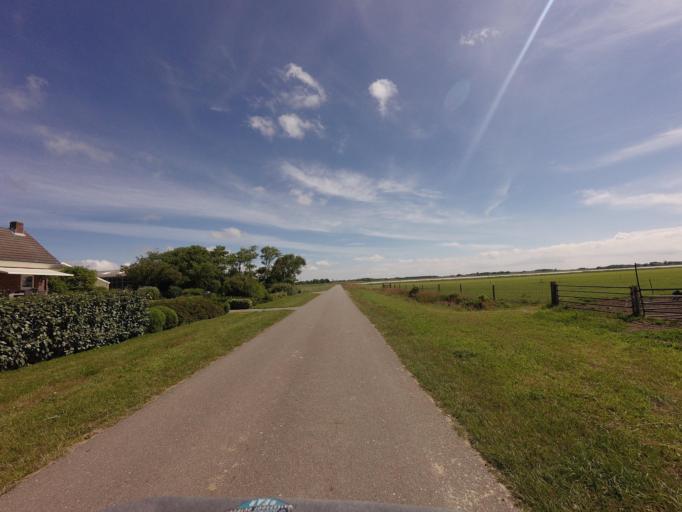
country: NL
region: North Holland
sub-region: Gemeente Texel
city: Den Burg
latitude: 53.0427
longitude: 4.7679
